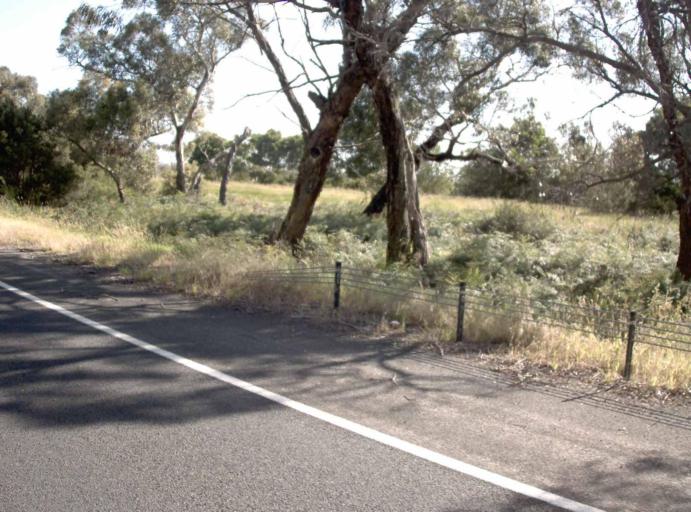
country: AU
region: Victoria
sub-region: Cardinia
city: Koo-Wee-Rup
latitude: -38.3417
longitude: 145.5581
